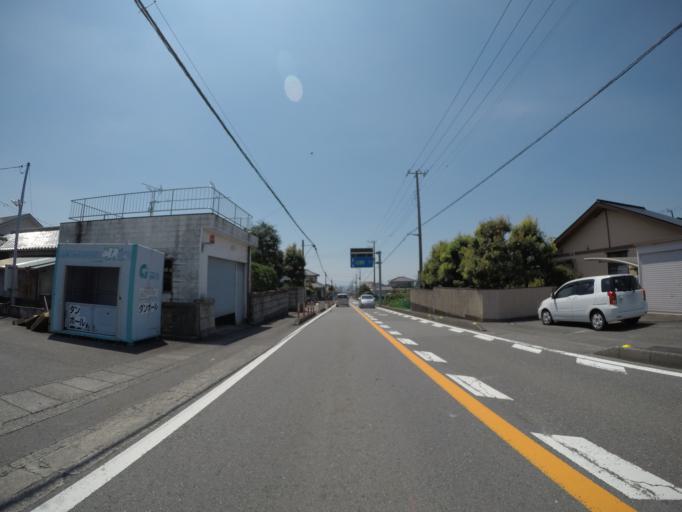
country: JP
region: Shizuoka
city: Fuji
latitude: 35.1933
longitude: 138.6796
